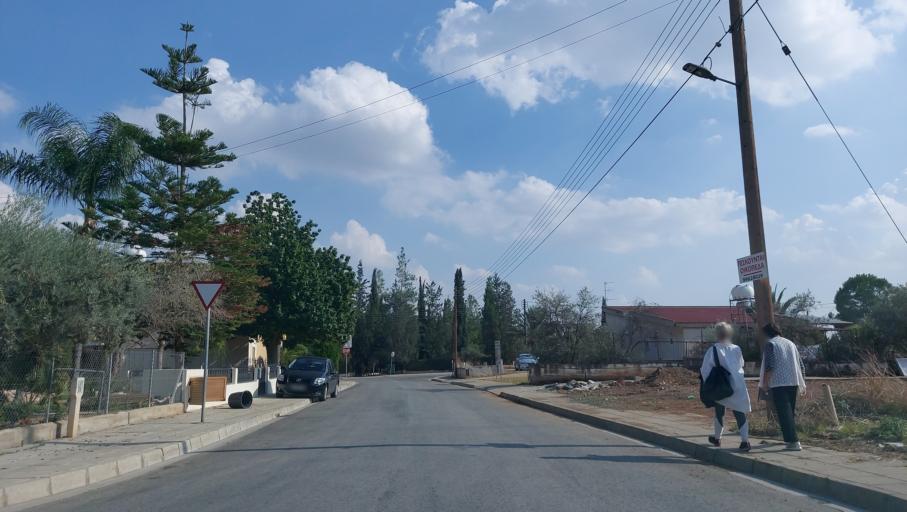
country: CY
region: Lefkosia
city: Tseri
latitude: 35.1081
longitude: 33.3088
